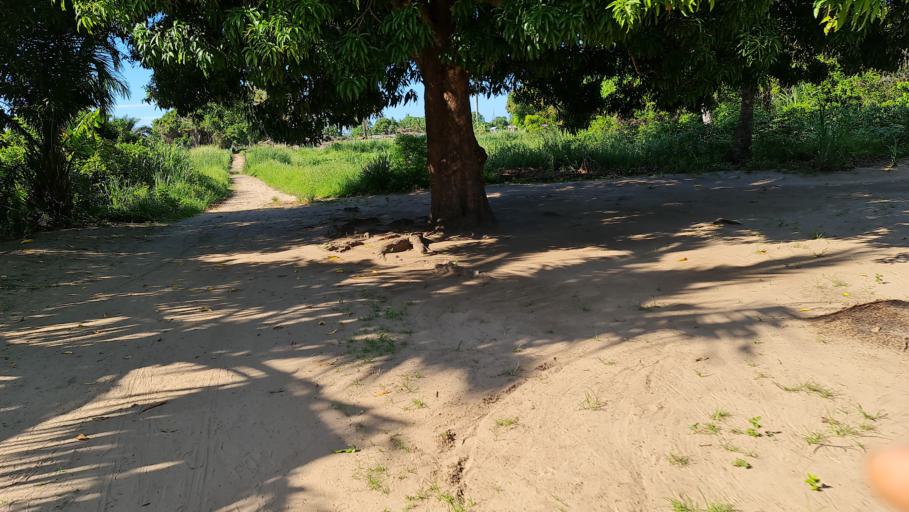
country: MZ
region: Zambezia
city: Quelimane
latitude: -17.4414
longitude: 37.6988
